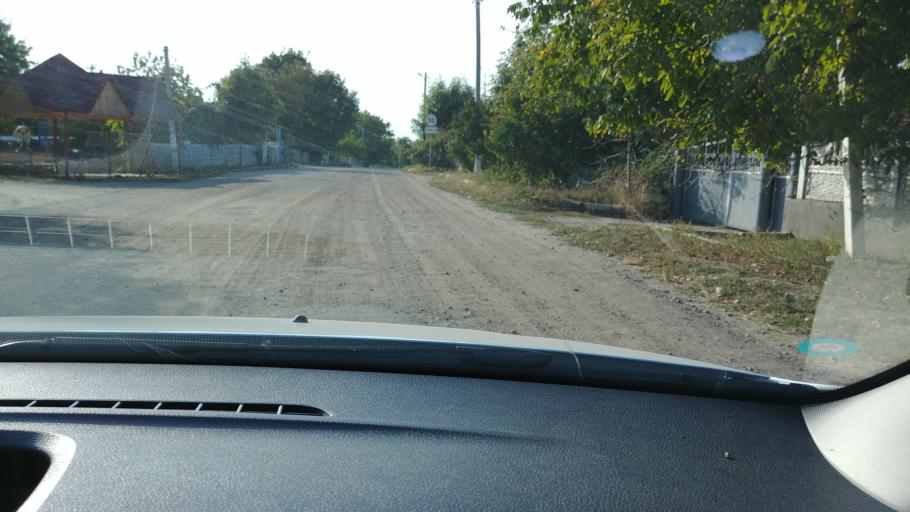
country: MD
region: Rezina
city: Rezina
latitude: 47.7452
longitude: 28.8914
